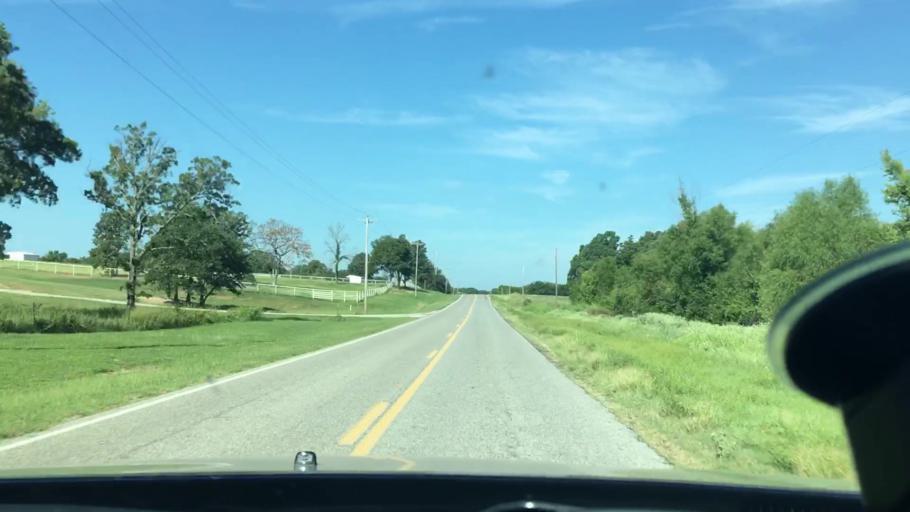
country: US
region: Oklahoma
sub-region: Johnston County
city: Tishomingo
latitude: 34.2733
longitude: -96.4371
